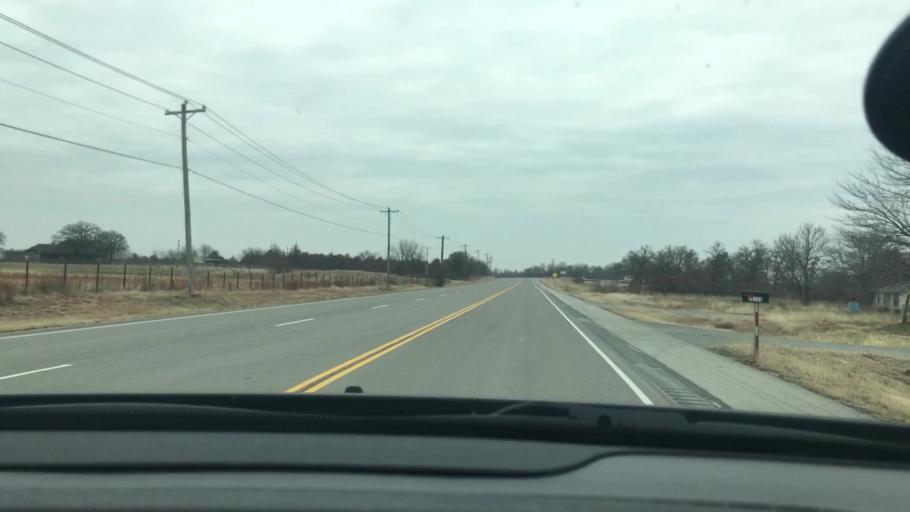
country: US
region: Oklahoma
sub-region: Carter County
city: Healdton
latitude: 34.3962
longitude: -97.5036
